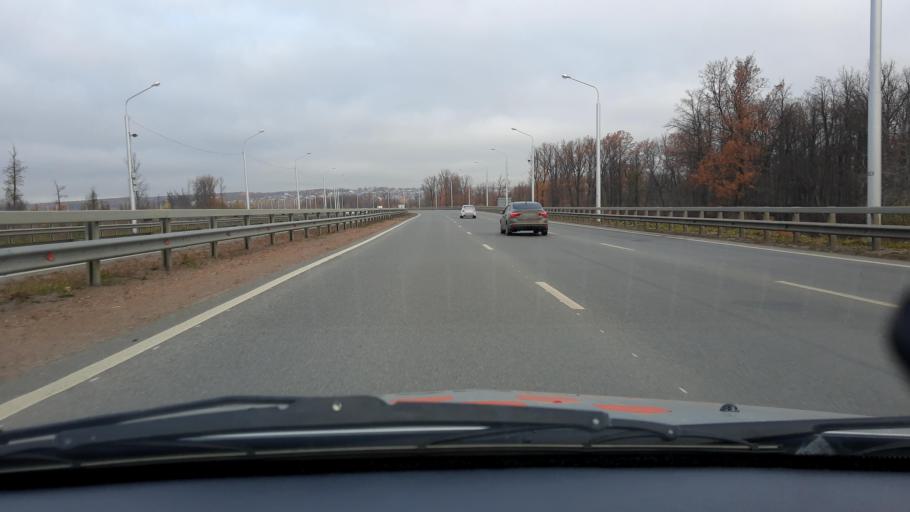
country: RU
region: Bashkortostan
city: Mikhaylovka
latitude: 54.7911
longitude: 55.9048
